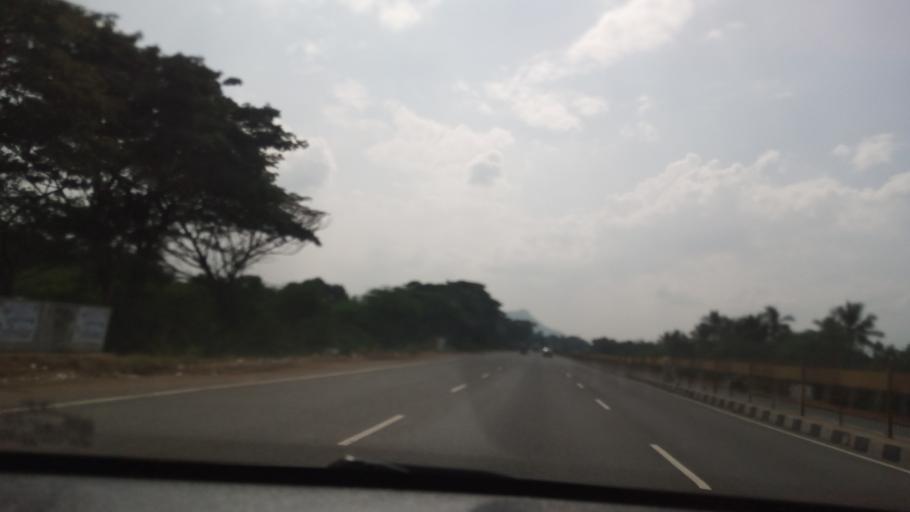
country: IN
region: Tamil Nadu
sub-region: Vellore
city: Pallikondai
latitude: 12.8970
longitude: 78.9208
